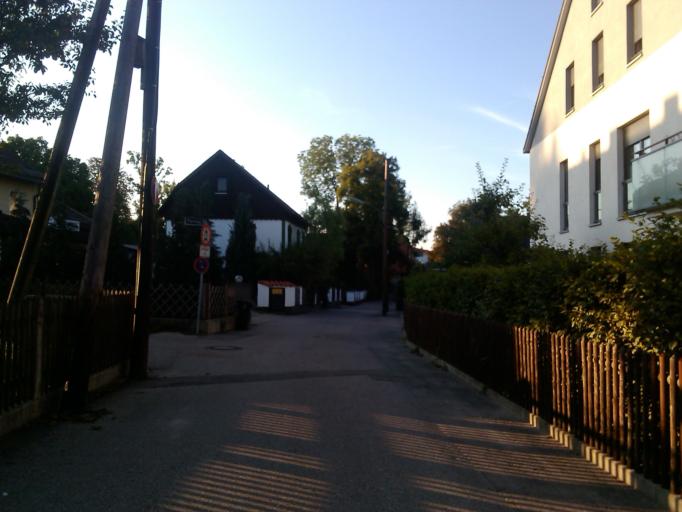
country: DE
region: Bavaria
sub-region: Upper Bavaria
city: Gauting
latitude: 48.0667
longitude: 11.3831
